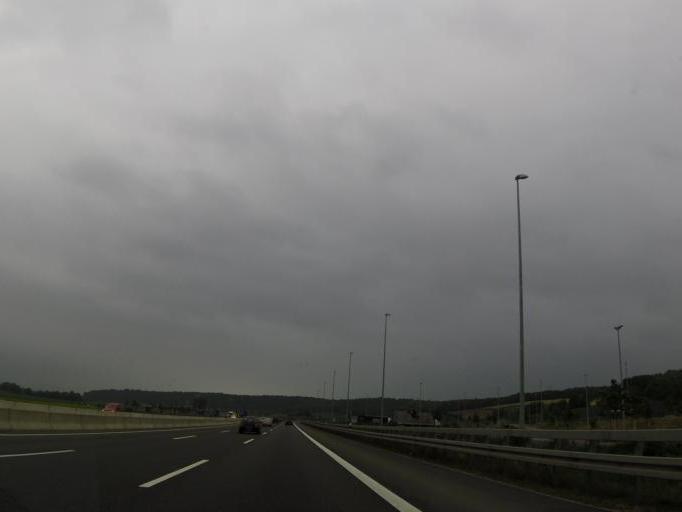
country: DE
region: Lower Saxony
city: Bovenden
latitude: 51.6067
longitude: 9.9065
